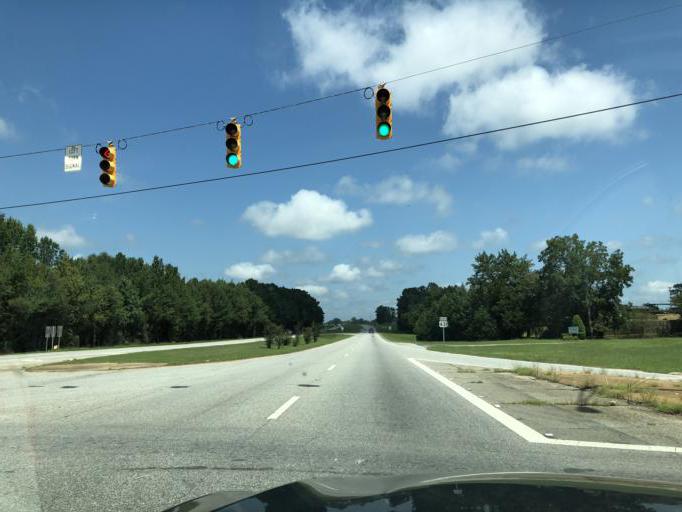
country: US
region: Alabama
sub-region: Henry County
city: Abbeville
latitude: 31.5886
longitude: -85.2784
